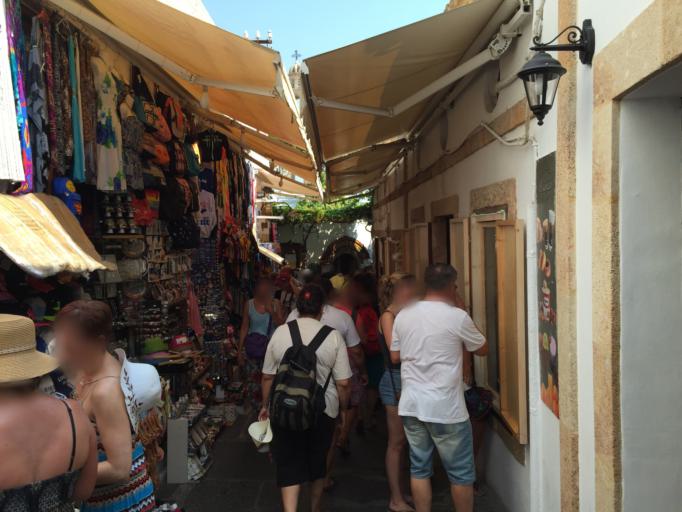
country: GR
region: South Aegean
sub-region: Nomos Dodekanisou
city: Lardos
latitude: 36.0913
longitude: 28.0858
